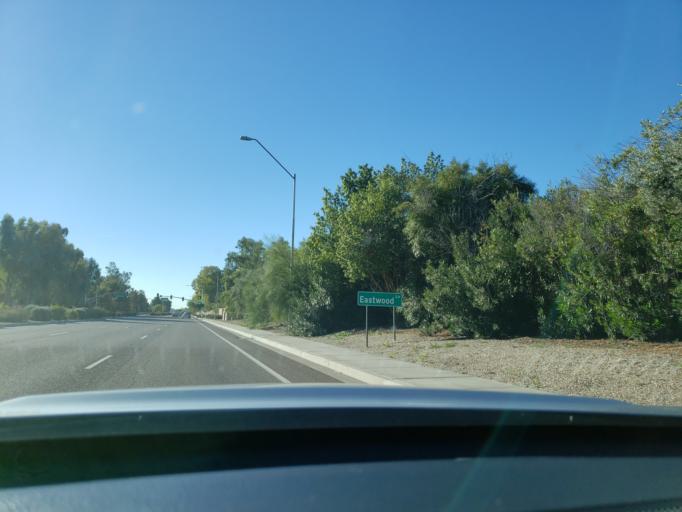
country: US
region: Arizona
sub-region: Maricopa County
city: Paradise Valley
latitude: 33.5619
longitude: -111.9262
